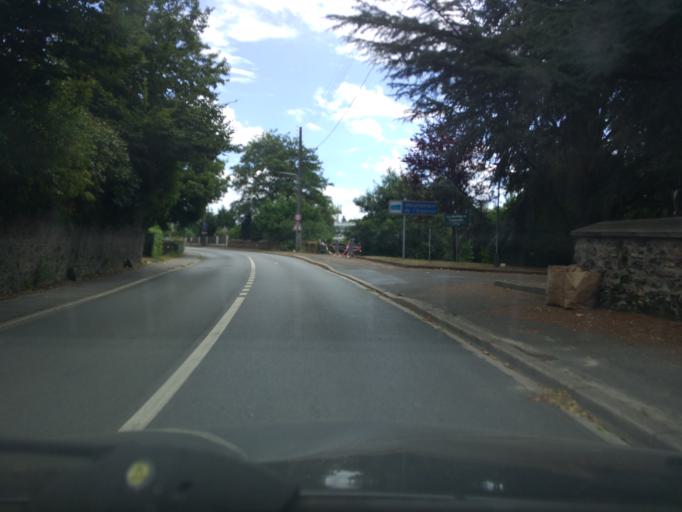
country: FR
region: Ile-de-France
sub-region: Departement des Yvelines
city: Saint-Remy-les-Chevreuse
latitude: 48.7034
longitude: 2.1037
